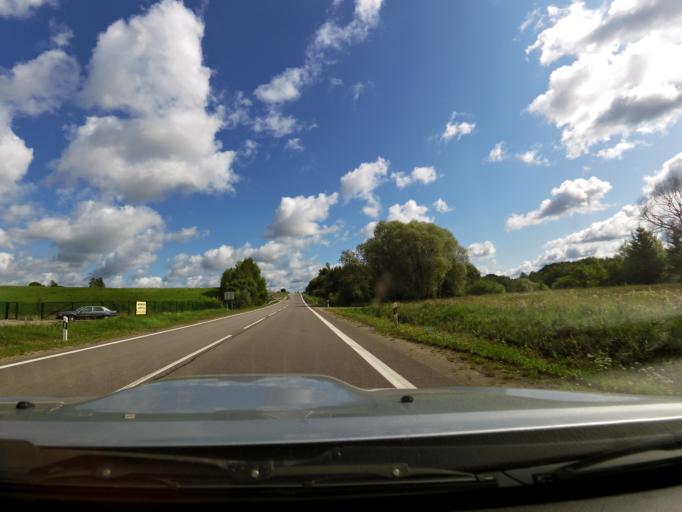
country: LT
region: Utenos apskritis
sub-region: Utena
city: Utena
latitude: 55.5175
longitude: 25.6557
